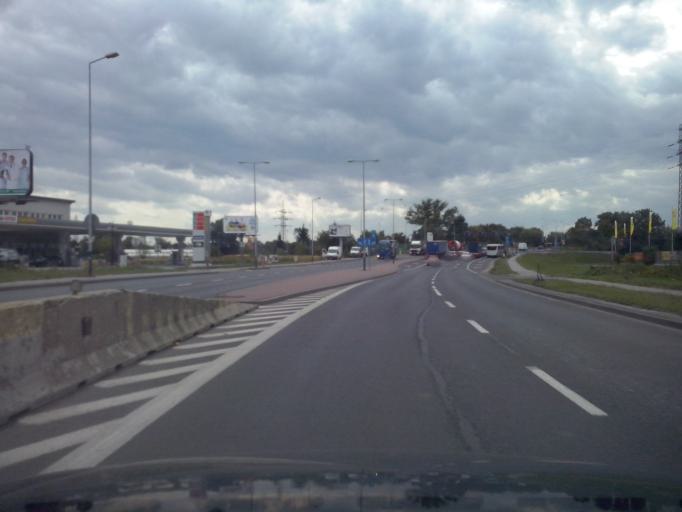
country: PL
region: Lesser Poland Voivodeship
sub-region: Krakow
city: Krakow
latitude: 50.0584
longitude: 20.0028
